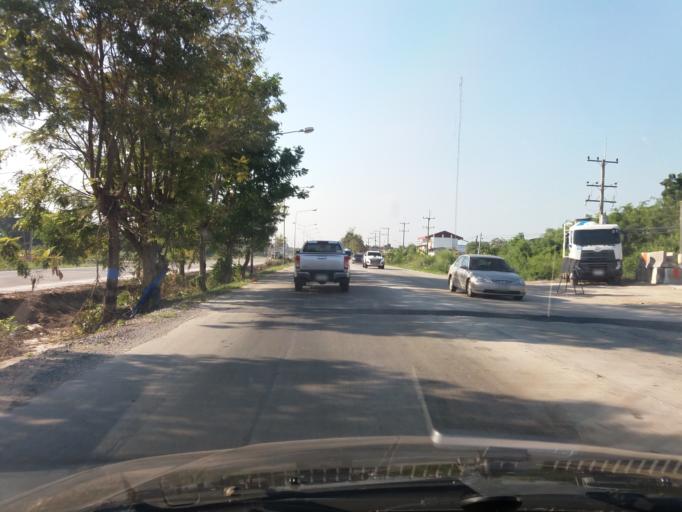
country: TH
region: Nakhon Sawan
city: Kao Liao
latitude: 15.7578
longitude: 99.9972
